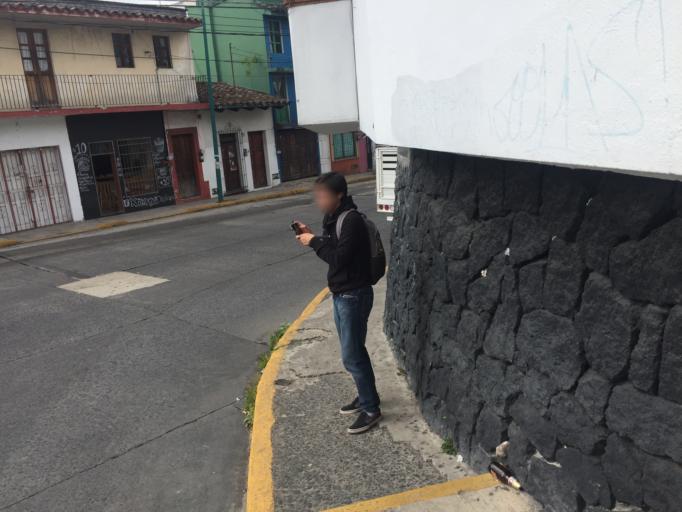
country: MX
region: Veracruz
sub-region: Xalapa
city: Xalapa de Enriquez
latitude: 19.5291
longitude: -96.9129
